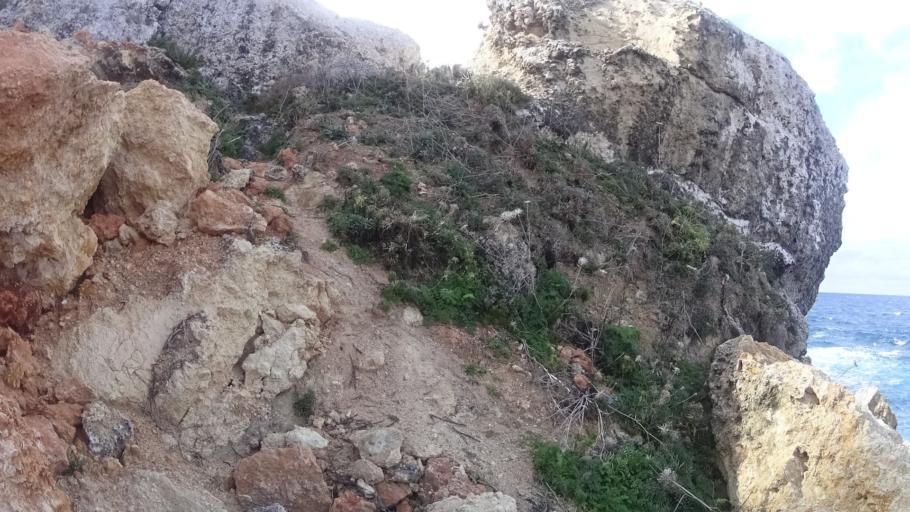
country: MT
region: Il-Mellieha
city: Mellieha
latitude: 35.9820
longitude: 14.3299
